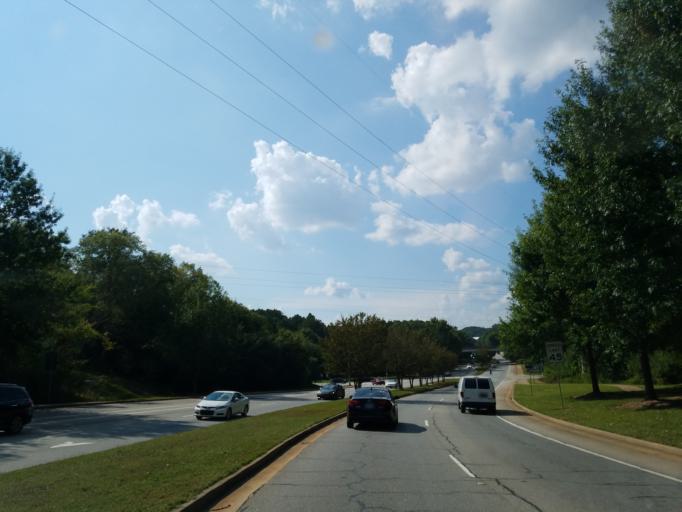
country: US
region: Georgia
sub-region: Clarke County
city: Athens
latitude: 33.9321
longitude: -83.3647
